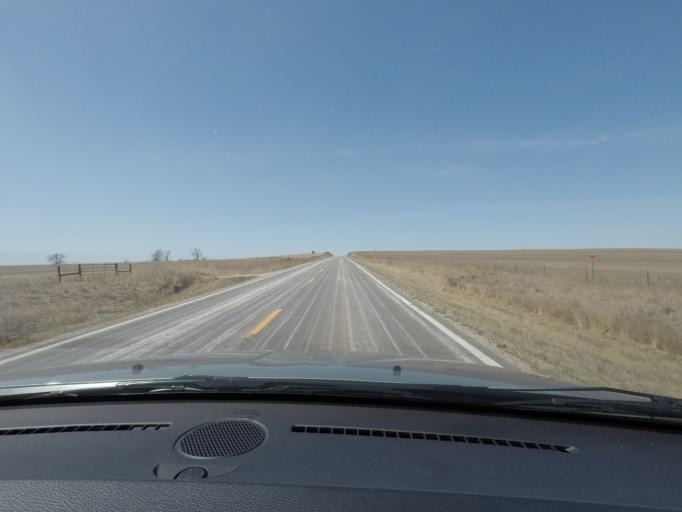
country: US
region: Kansas
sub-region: Morris County
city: Council Grove
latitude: 38.6590
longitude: -96.2324
